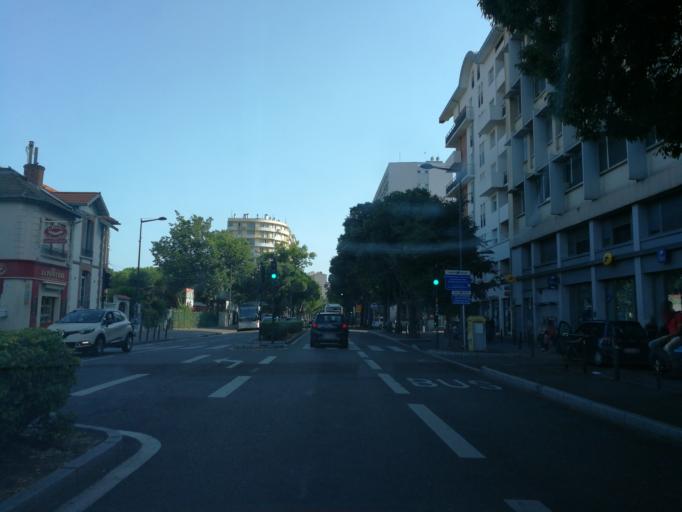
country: FR
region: Midi-Pyrenees
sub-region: Departement de la Haute-Garonne
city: Toulouse
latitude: 43.6261
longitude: 1.4339
